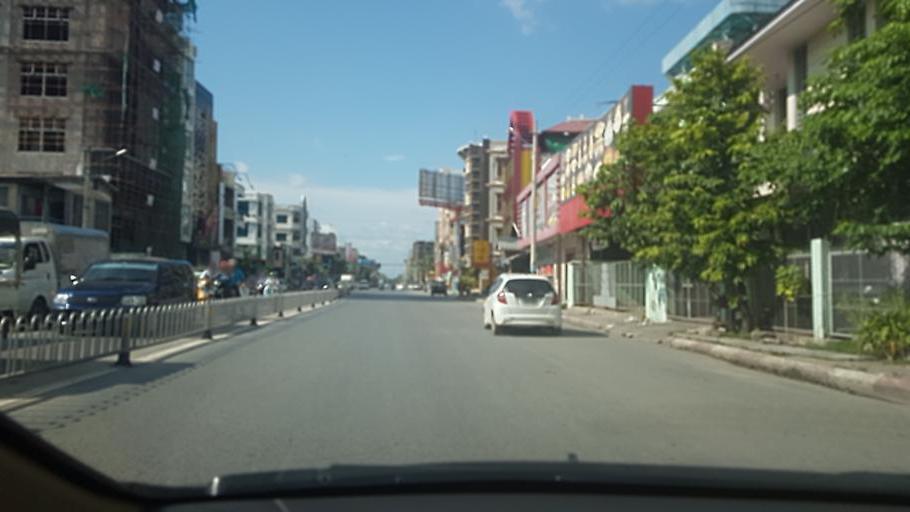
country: MM
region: Mandalay
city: Mandalay
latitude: 21.9693
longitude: 96.0865
